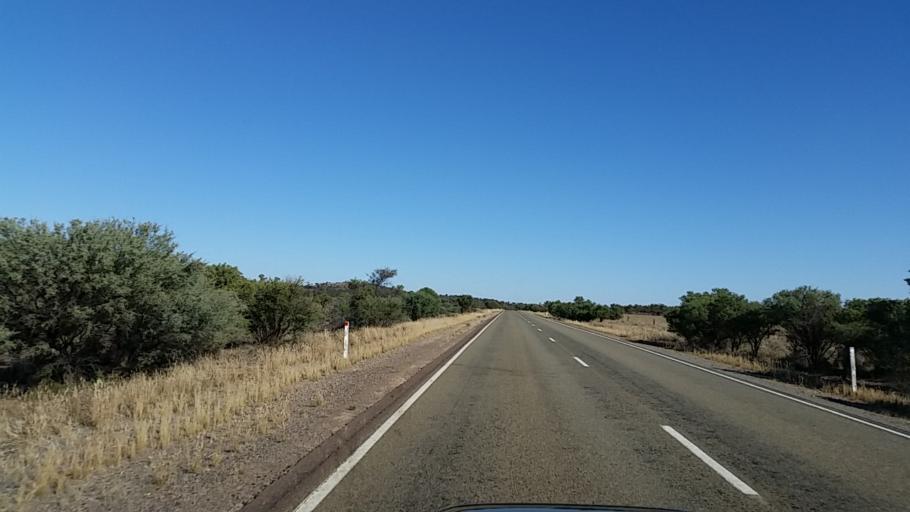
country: AU
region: South Australia
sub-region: Flinders Ranges
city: Quorn
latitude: -32.4936
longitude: 138.5470
